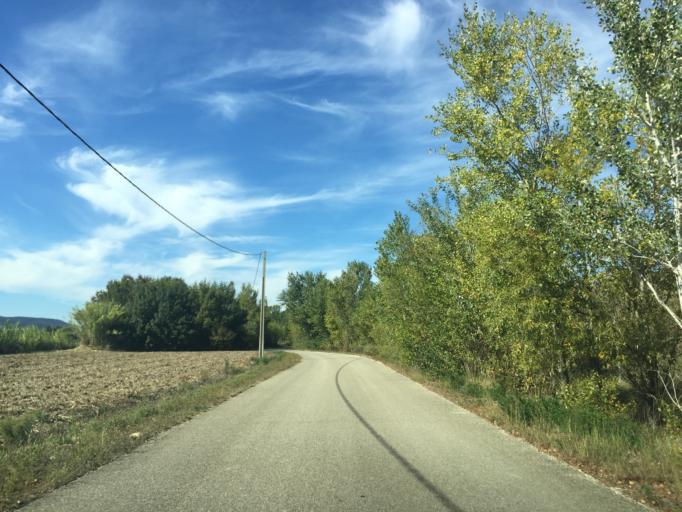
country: FR
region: Provence-Alpes-Cote d'Azur
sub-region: Departement du Vaucluse
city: Piolenc
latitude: 44.1622
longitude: 4.7363
